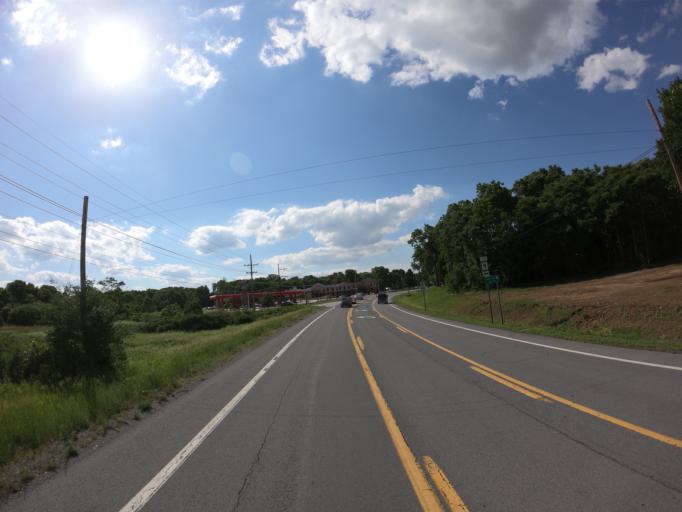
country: US
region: West Virginia
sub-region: Berkeley County
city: Martinsburg
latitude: 39.4012
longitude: -77.9105
